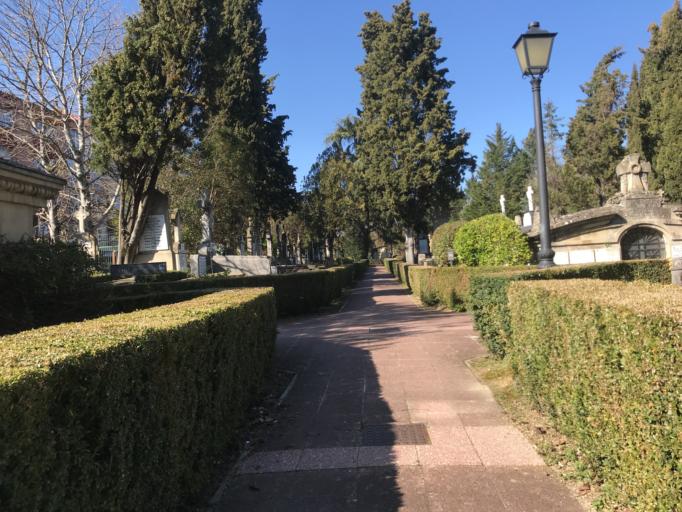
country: ES
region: Basque Country
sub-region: Provincia de Alava
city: Gasteiz / Vitoria
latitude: 42.8592
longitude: -2.6737
